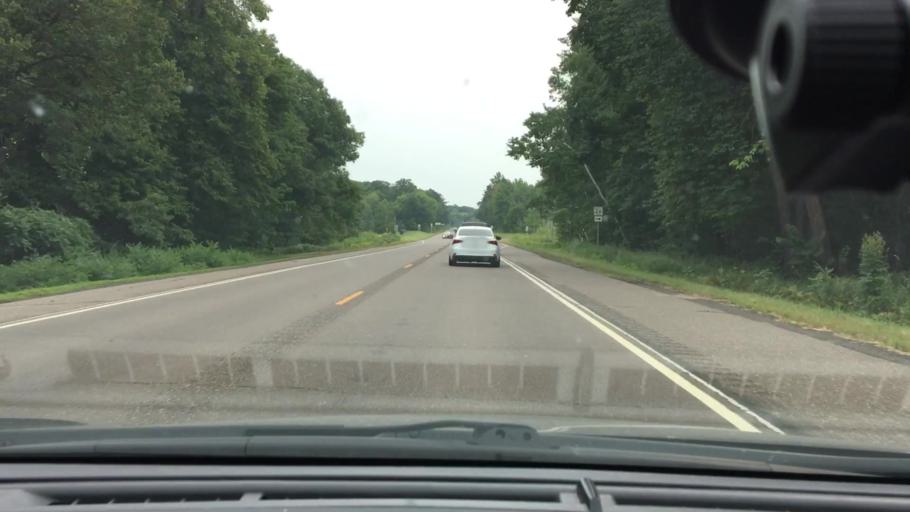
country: US
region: Minnesota
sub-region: Mille Lacs County
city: Vineland
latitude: 46.1461
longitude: -93.7265
